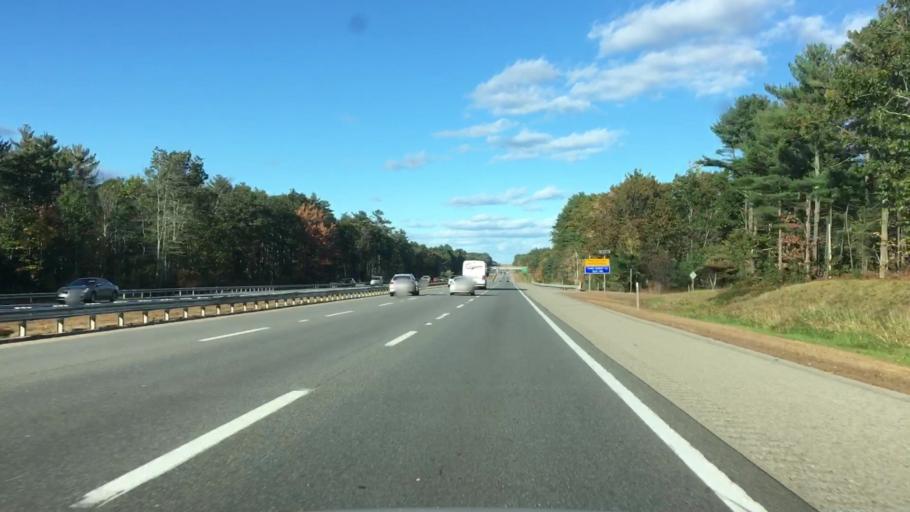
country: US
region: Maine
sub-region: York County
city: West Kennebunk
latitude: 43.3717
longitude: -70.5810
